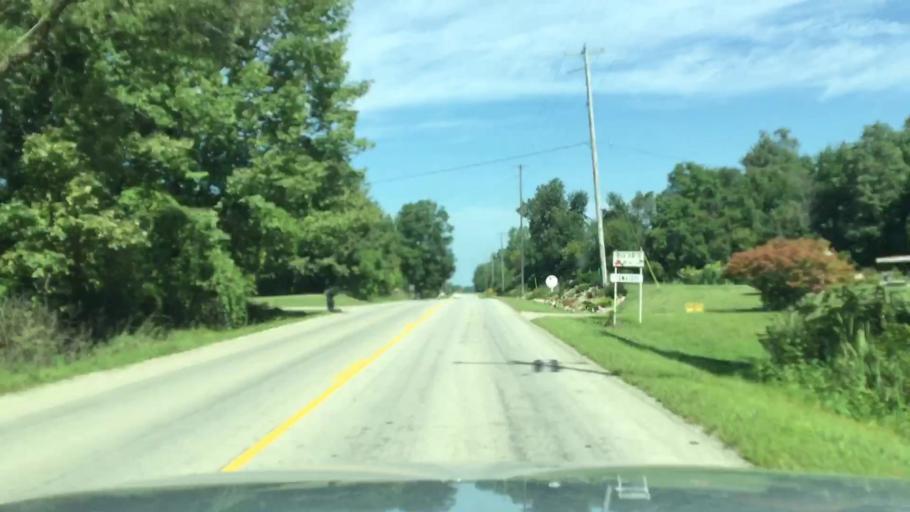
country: US
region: Michigan
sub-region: Lenawee County
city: Manitou Beach-Devils Lake
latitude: 42.0064
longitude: -84.2760
